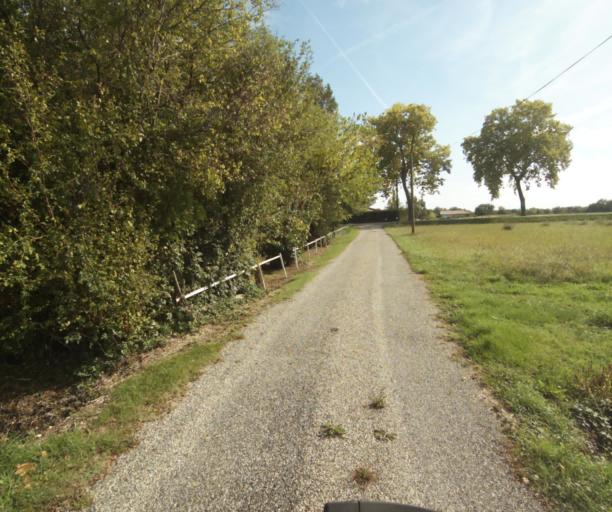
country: FR
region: Midi-Pyrenees
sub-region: Departement du Tarn-et-Garonne
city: Saint-Porquier
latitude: 43.9430
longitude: 1.1366
